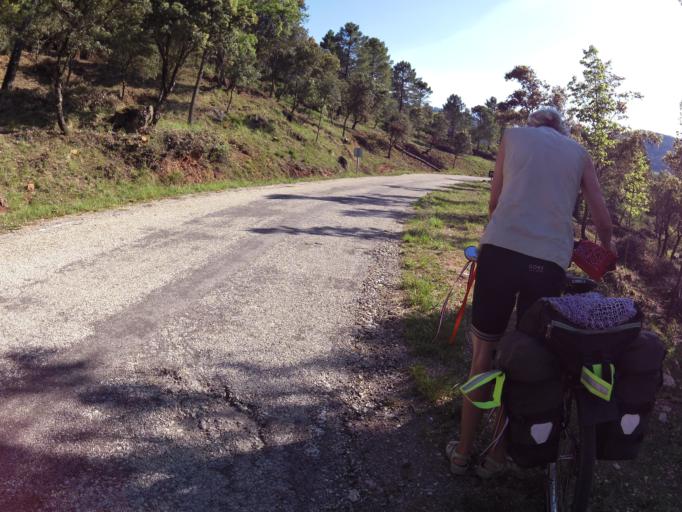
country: ES
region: Castille-La Mancha
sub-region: Provincia de Albacete
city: Riopar
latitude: 38.5185
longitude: -2.4555
